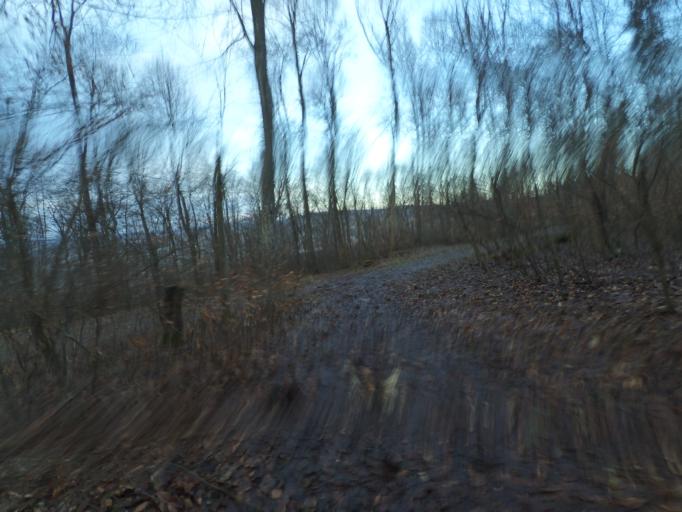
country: DE
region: Baden-Wuerttemberg
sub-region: Regierungsbezirk Stuttgart
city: Aalen
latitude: 48.8180
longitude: 10.0909
